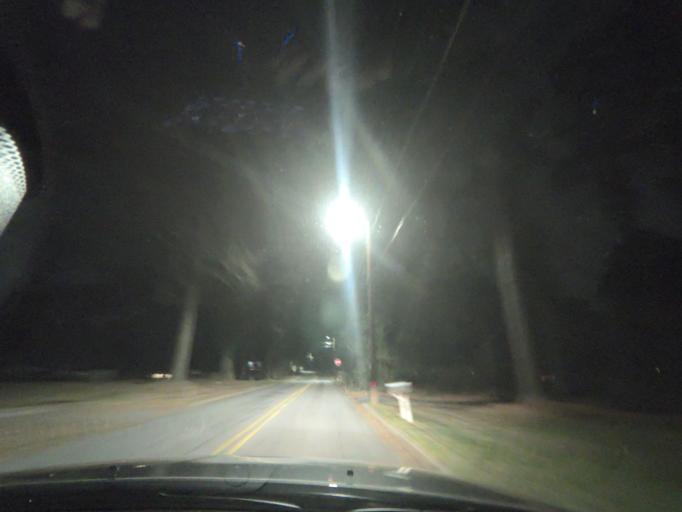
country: US
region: Georgia
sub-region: Fulton County
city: East Point
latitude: 33.6855
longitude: -84.4800
